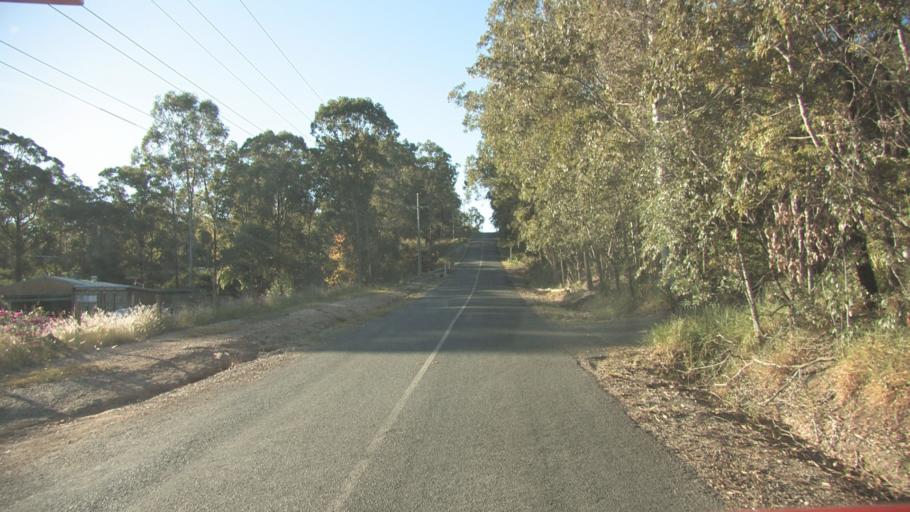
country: AU
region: Queensland
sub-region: Logan
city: Chambers Flat
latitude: -27.7664
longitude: 153.1223
